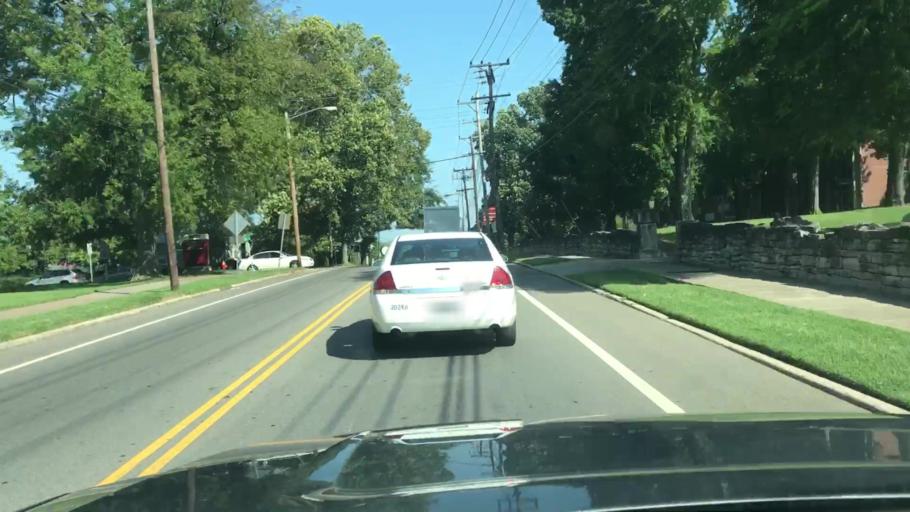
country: US
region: Tennessee
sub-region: Davidson County
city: Nashville
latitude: 36.1678
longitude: -86.8059
